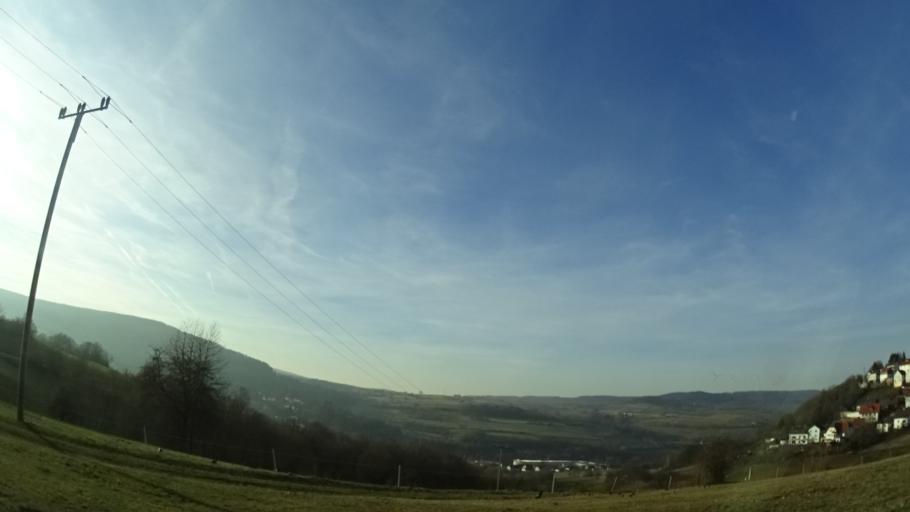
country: DE
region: Bavaria
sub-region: Regierungsbezirk Unterfranken
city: Zeitlofs
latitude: 50.2959
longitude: 9.6702
